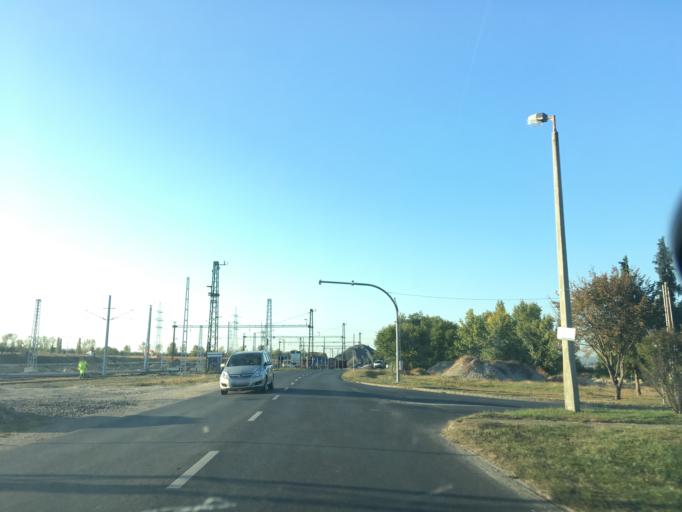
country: HU
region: Pest
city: Szazhalombatta
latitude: 47.3242
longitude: 18.8988
